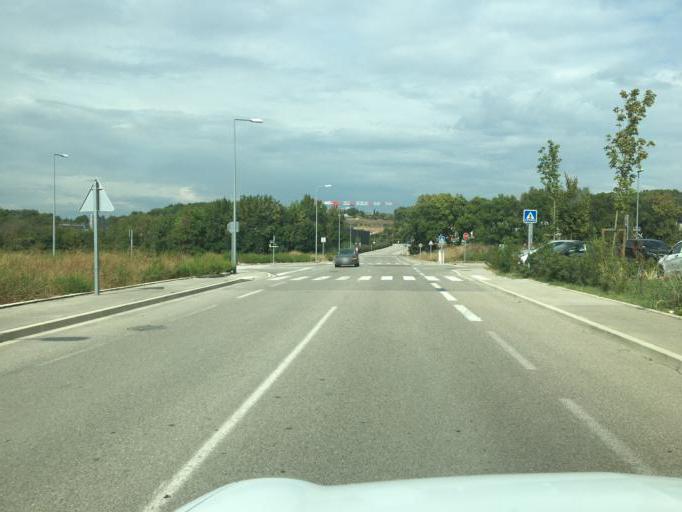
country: FR
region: Provence-Alpes-Cote d'Azur
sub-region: Departement des Bouches-du-Rhone
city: Bouc-Bel-Air
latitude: 43.4797
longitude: 5.3941
